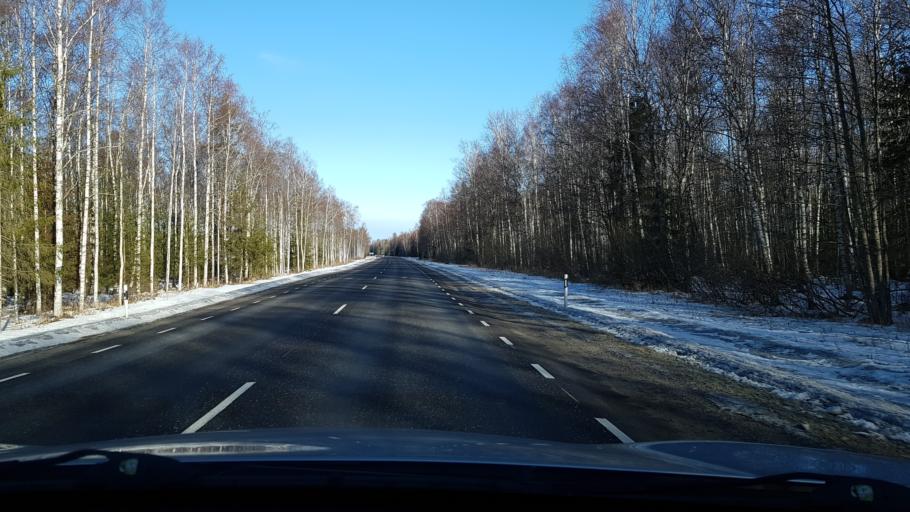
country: EE
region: Viljandimaa
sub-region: Vohma linn
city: Vohma
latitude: 58.5980
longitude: 25.5725
